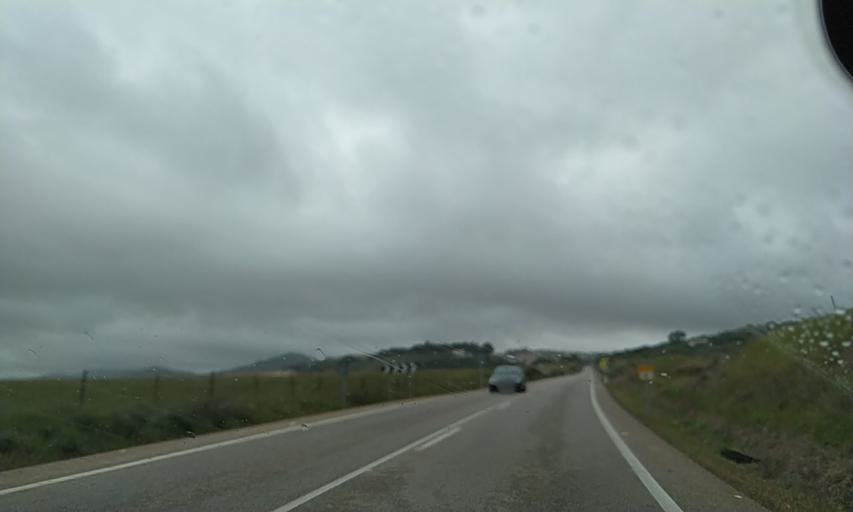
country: ES
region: Extremadura
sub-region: Provincia de Caceres
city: Caceres
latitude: 39.4945
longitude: -6.3856
